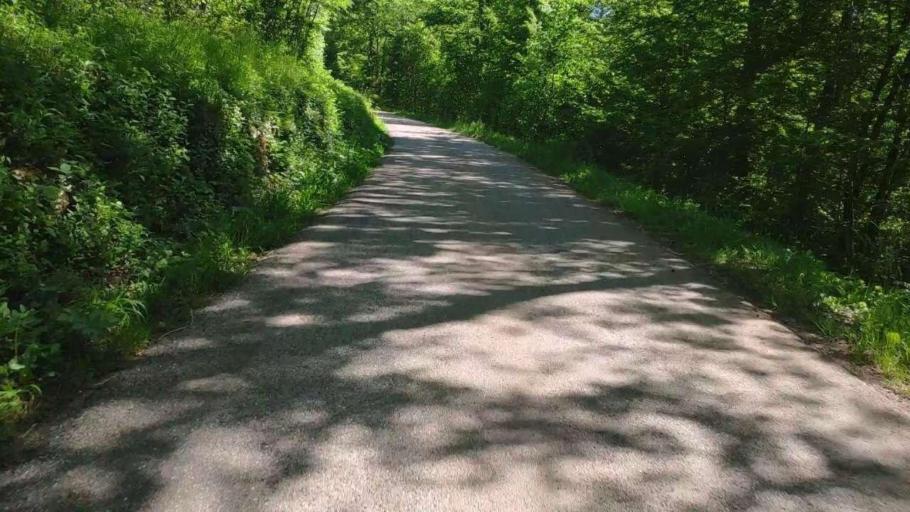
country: FR
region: Franche-Comte
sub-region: Departement du Jura
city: Poligny
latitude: 46.7437
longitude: 5.7734
